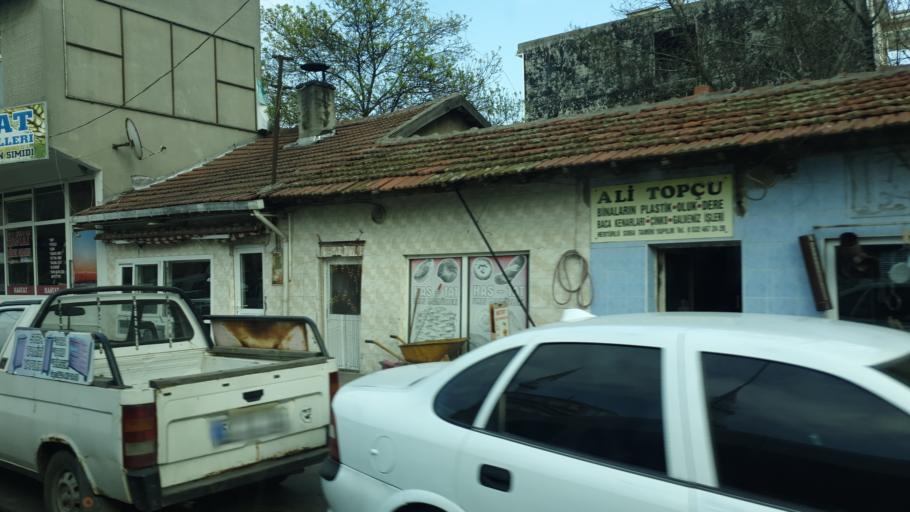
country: TR
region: Tekirdag
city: Muratli
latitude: 41.1744
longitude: 27.4998
